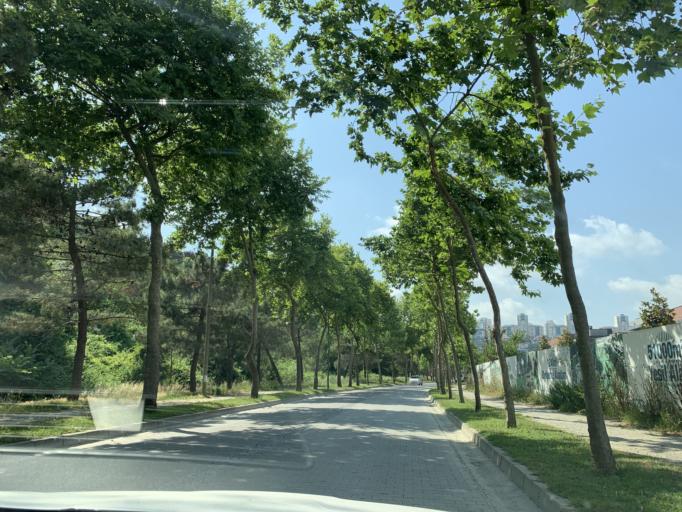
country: TR
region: Istanbul
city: Esenyurt
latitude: 41.0647
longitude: 28.6952
